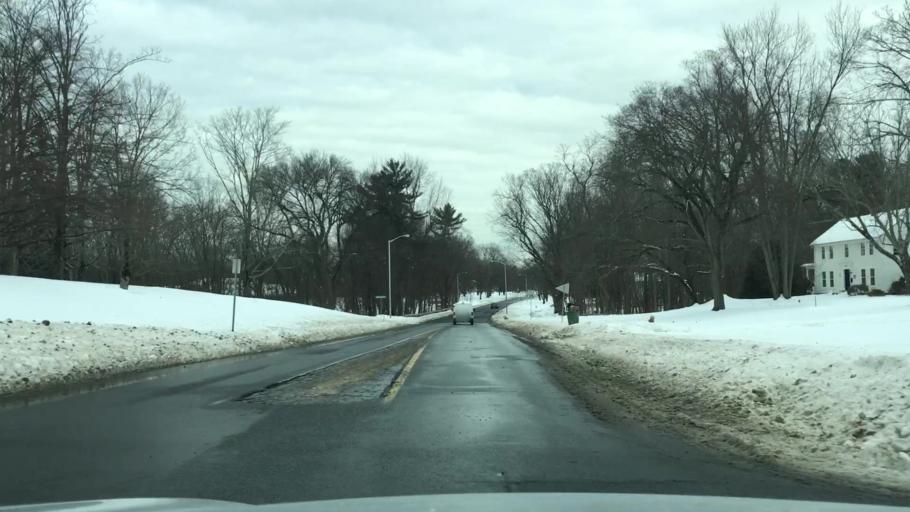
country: US
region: Massachusetts
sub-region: Hampden County
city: Longmeadow
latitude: 42.0525
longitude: -72.5824
